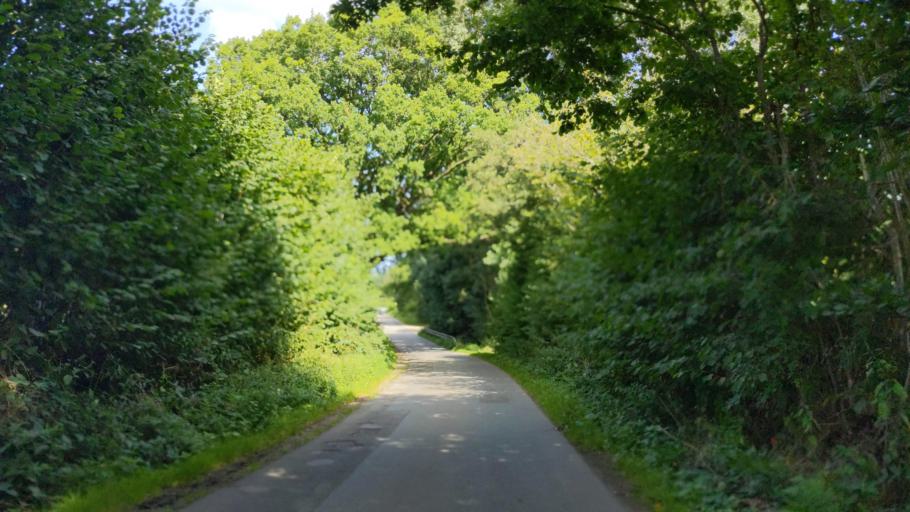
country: DE
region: Schleswig-Holstein
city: Altenkrempe
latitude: 54.1571
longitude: 10.8083
